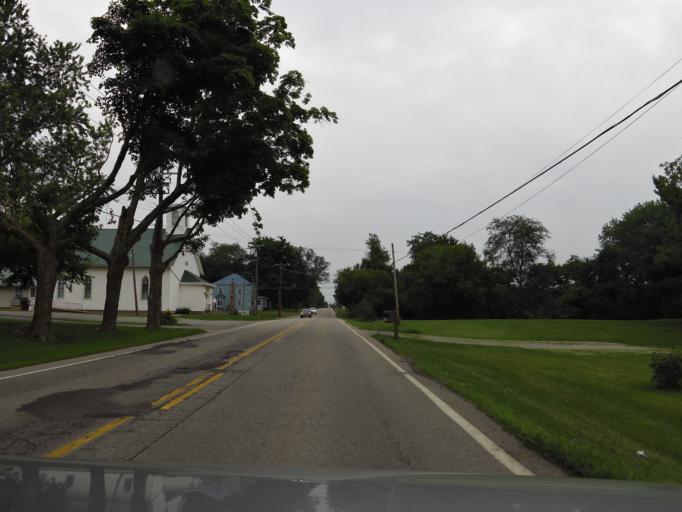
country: US
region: Ohio
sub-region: Clinton County
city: Blanchester
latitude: 39.2795
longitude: -83.9094
